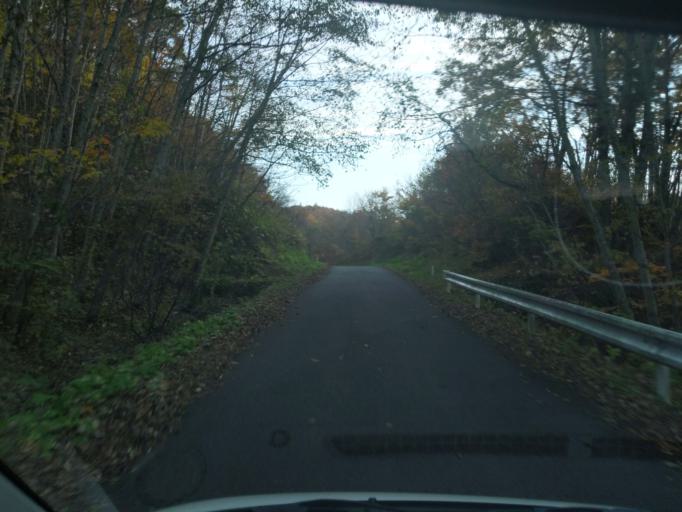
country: JP
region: Iwate
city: Ichinoseki
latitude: 38.9954
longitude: 141.0054
